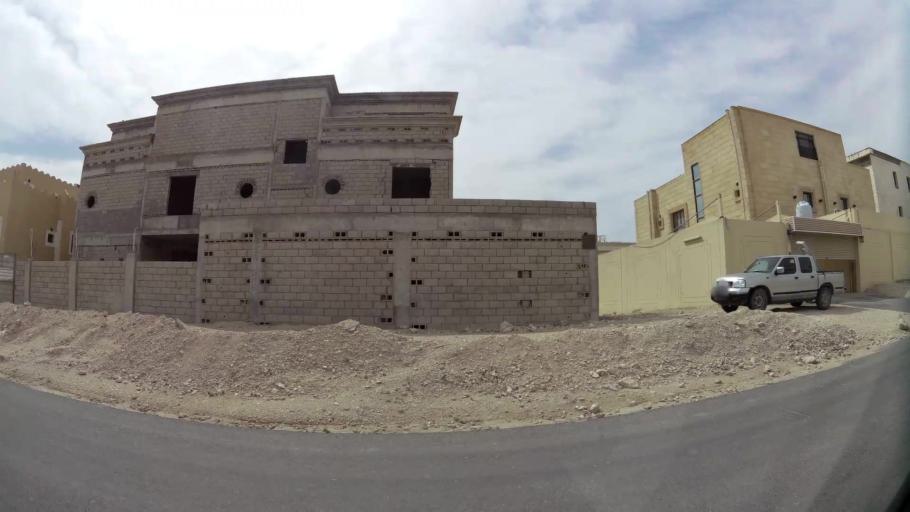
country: QA
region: Baladiyat ad Dawhah
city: Doha
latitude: 25.2118
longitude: 51.4909
